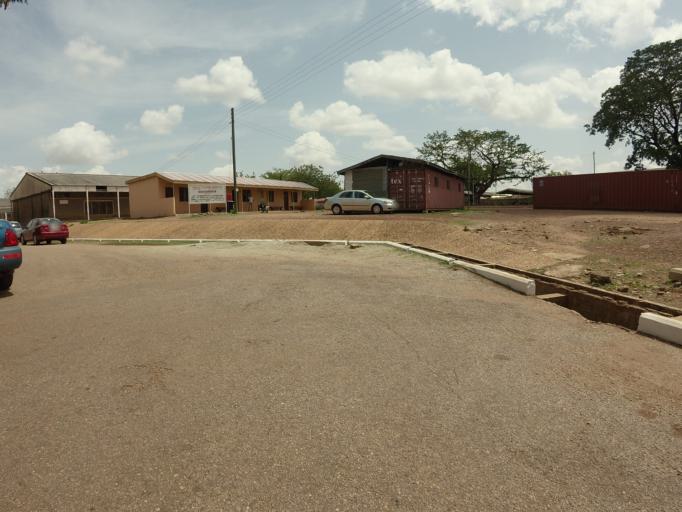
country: GH
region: Northern
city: Tamale
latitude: 9.3933
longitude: -0.8242
